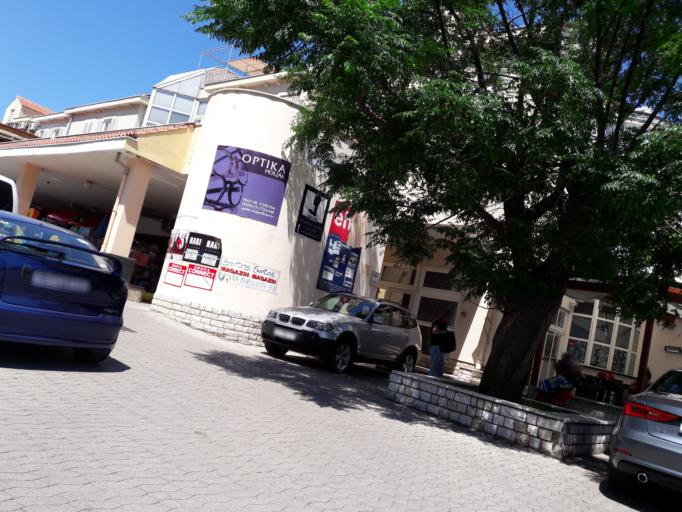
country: HR
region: Primorsko-Goranska
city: Banjol
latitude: 44.7606
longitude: 14.7602
